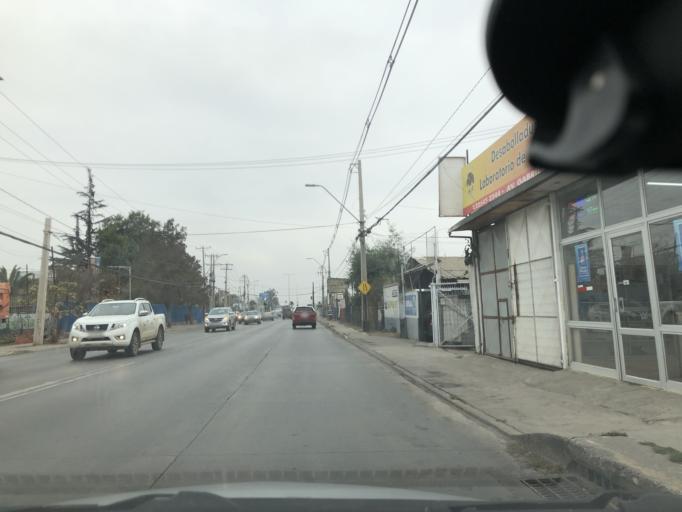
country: CL
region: Santiago Metropolitan
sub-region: Provincia de Santiago
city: La Pintana
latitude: -33.5828
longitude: -70.6078
